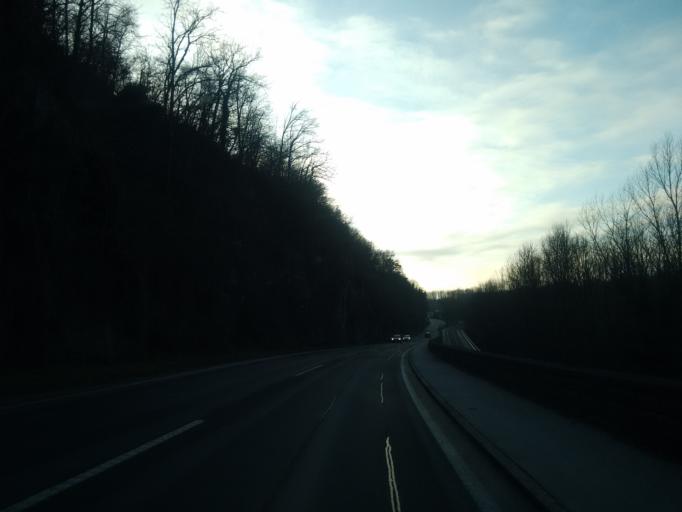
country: AT
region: Lower Austria
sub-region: Politischer Bezirk Melk
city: Melk
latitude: 48.2324
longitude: 15.3394
